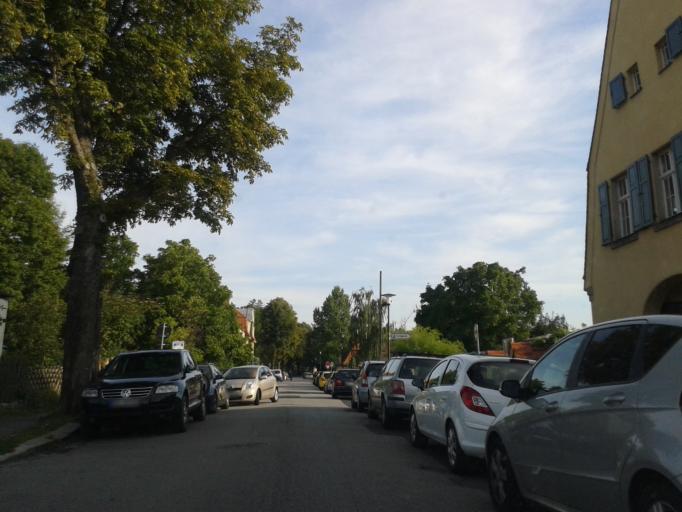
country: DE
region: Saxony
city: Albertstadt
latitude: 51.0532
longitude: 13.8146
